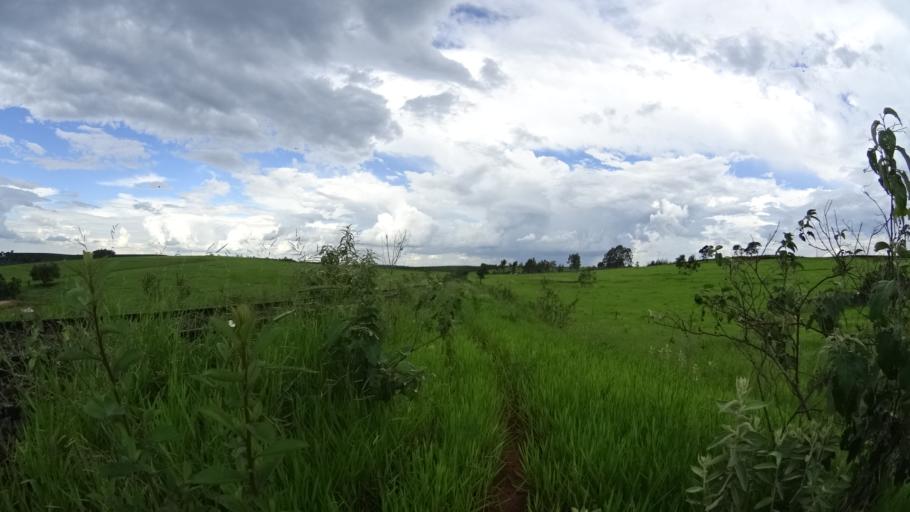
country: BR
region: Sao Paulo
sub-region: Marilia
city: Marilia
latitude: -22.2168
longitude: -49.8698
